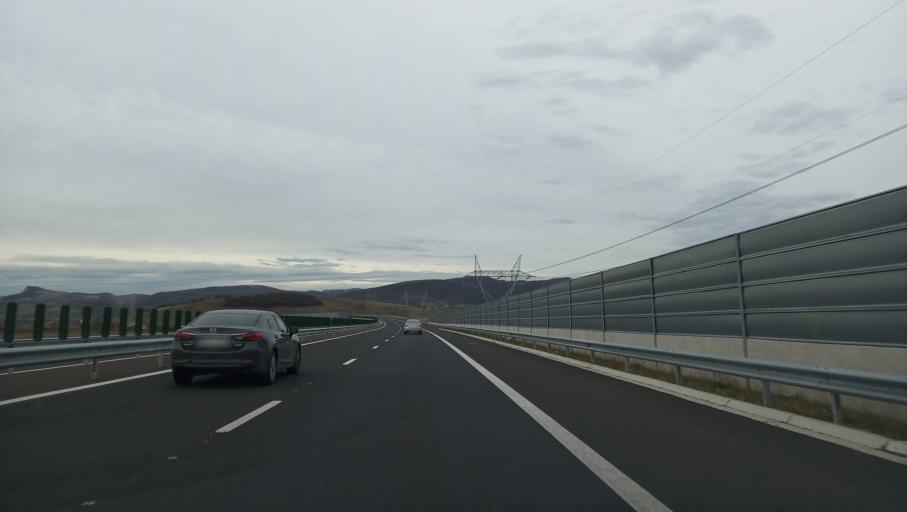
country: RO
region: Hunedoara
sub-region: Comuna Branisca
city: Branisca
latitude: 45.9189
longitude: 22.7816
